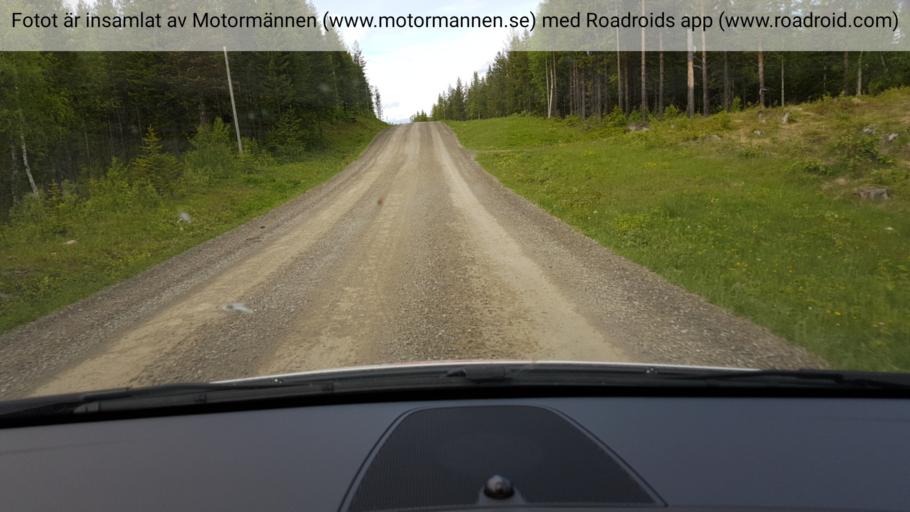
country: SE
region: Jaemtland
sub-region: Bergs Kommun
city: Hoverberg
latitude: 62.9961
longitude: 14.1541
